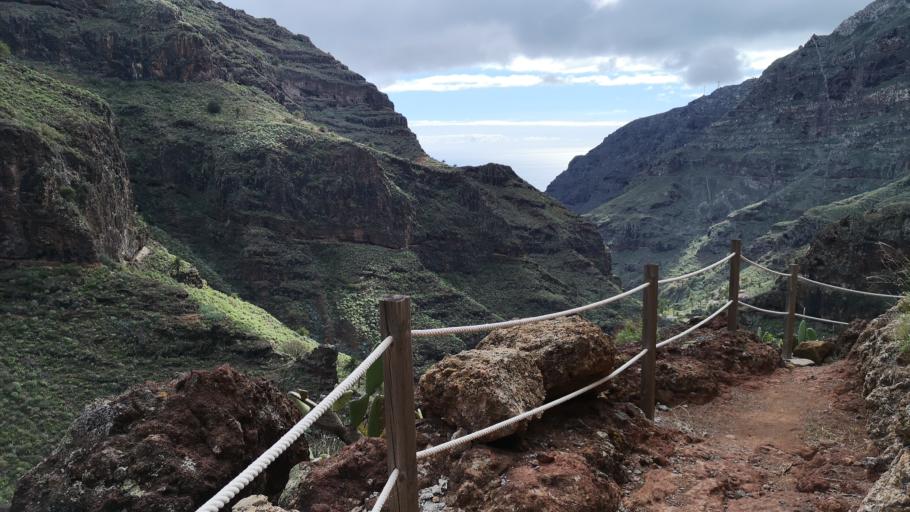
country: ES
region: Canary Islands
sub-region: Provincia de Santa Cruz de Tenerife
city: Alajero
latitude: 28.0763
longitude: -17.2297
